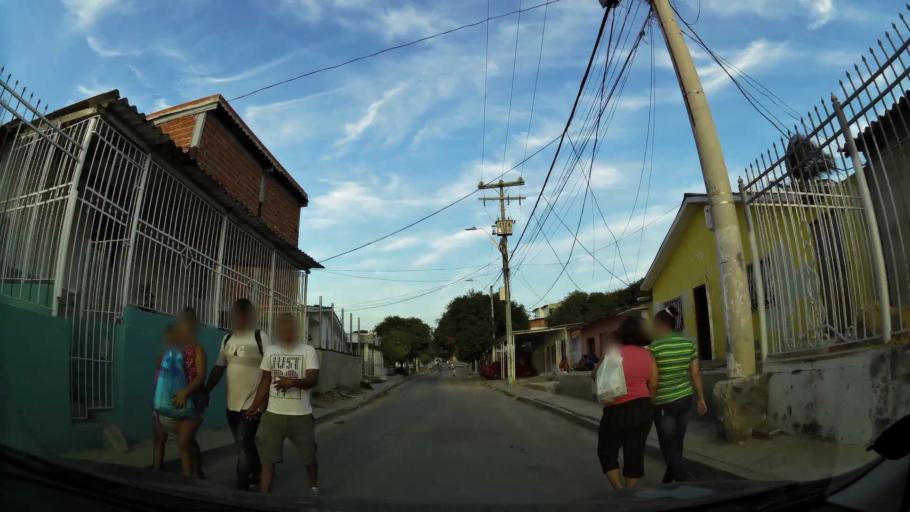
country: CO
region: Atlantico
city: Barranquilla
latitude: 10.9466
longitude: -74.8215
